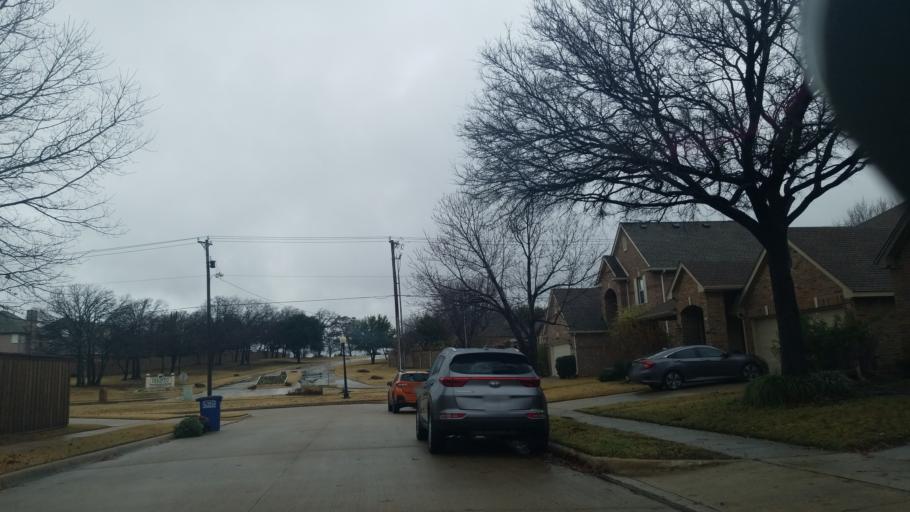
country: US
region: Texas
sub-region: Denton County
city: Corinth
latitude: 33.1516
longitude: -97.0845
